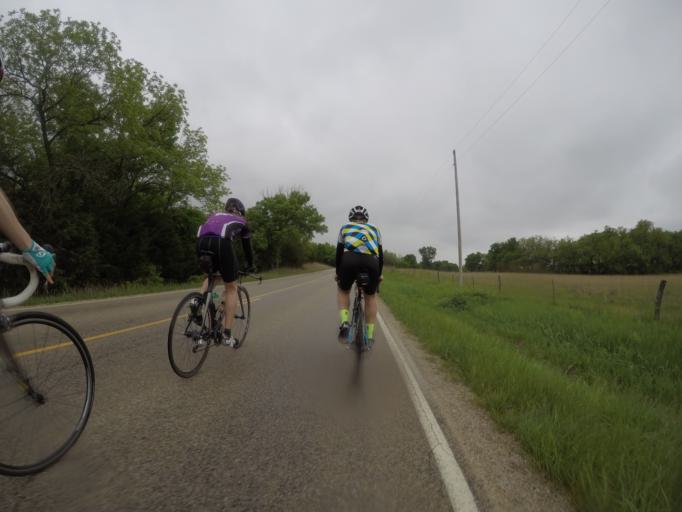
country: US
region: Kansas
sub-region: Pottawatomie County
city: Westmoreland
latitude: 39.4712
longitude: -96.1839
